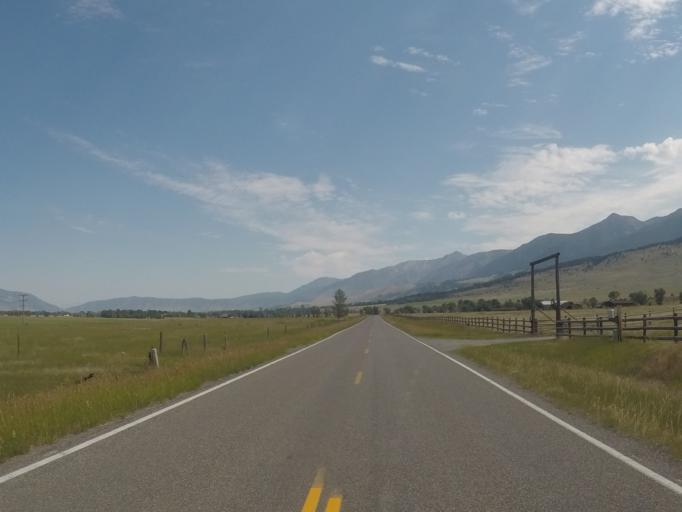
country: US
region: Montana
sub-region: Park County
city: Livingston
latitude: 45.4272
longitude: -110.6200
